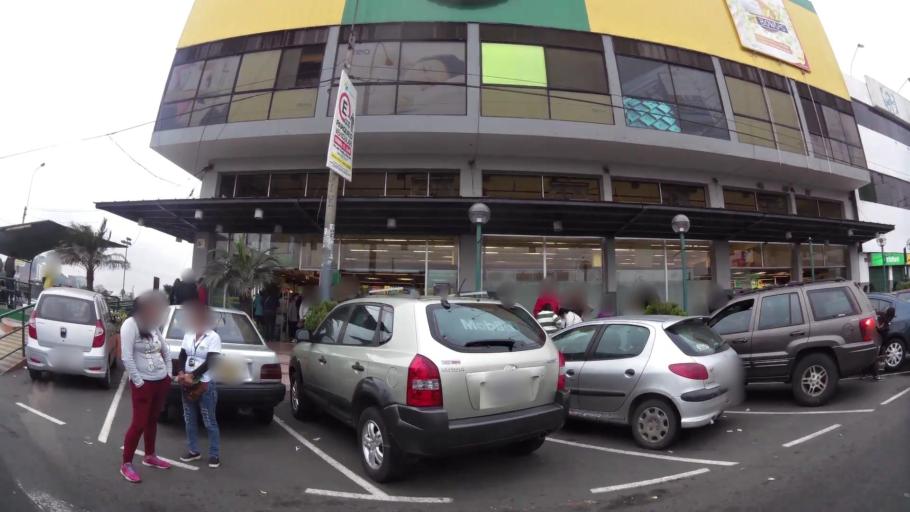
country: PE
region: Lima
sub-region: Lima
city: La Molina
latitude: -12.0700
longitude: -76.9576
